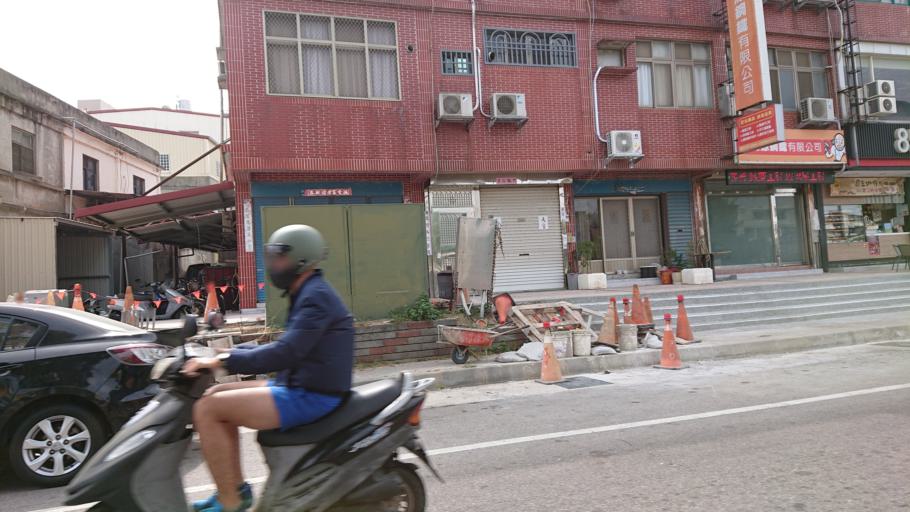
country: TW
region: Fukien
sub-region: Kinmen
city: Jincheng
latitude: 24.4402
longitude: 118.4148
